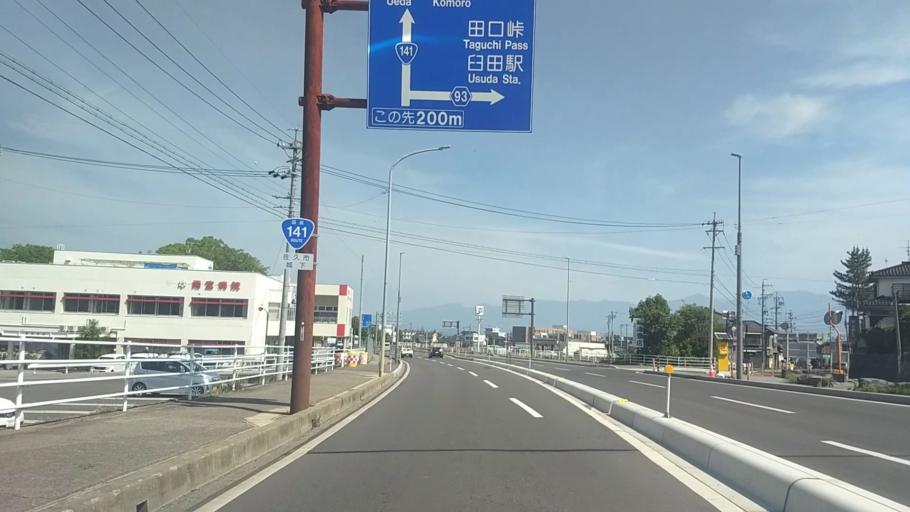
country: JP
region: Nagano
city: Saku
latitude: 36.1913
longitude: 138.4799
